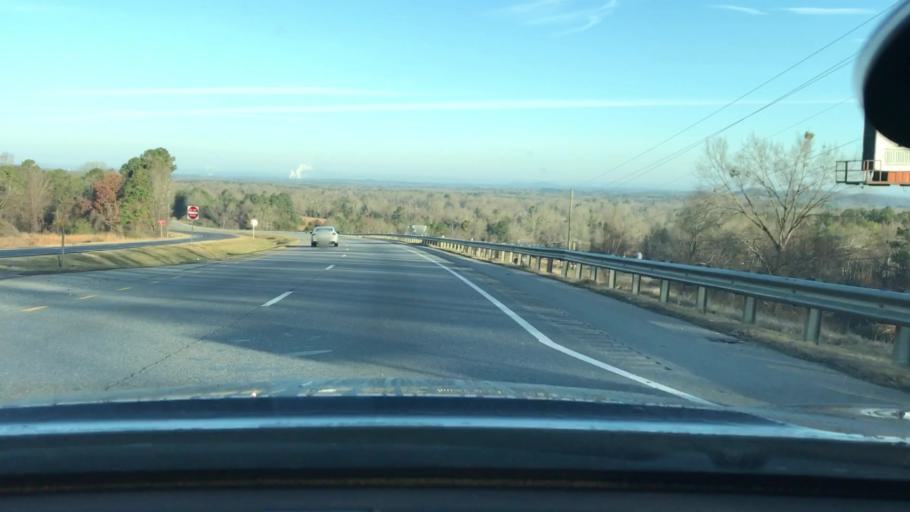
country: US
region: Alabama
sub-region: Talladega County
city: Mignon
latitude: 33.2035
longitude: -86.3075
